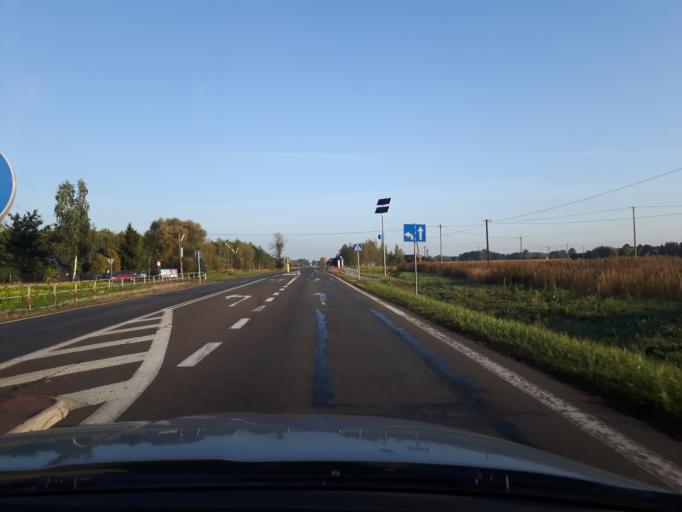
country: PL
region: Masovian Voivodeship
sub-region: Powiat plonski
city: Baboszewo
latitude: 52.7229
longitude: 20.3249
